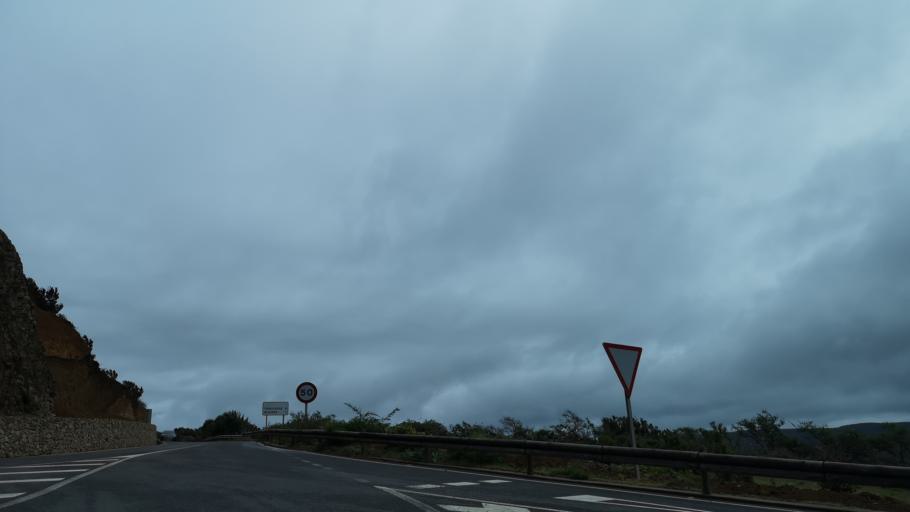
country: ES
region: Canary Islands
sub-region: Provincia de Santa Cruz de Tenerife
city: Vallehermosa
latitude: 28.1650
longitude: -17.2962
